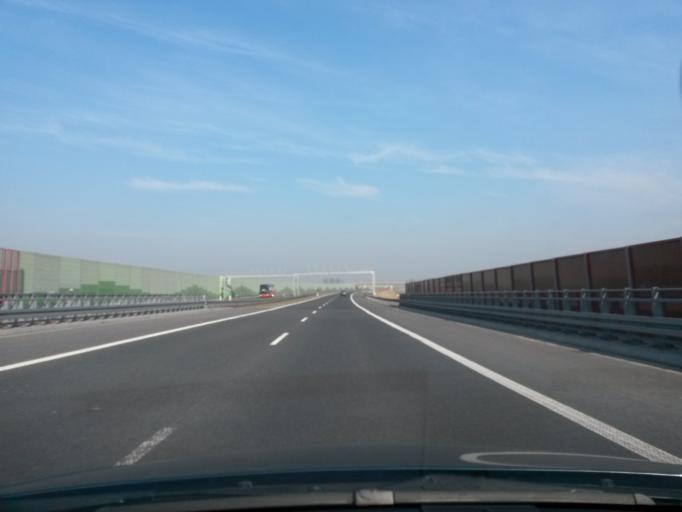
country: PL
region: Lodz Voivodeship
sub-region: Powiat kutnowski
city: Krzyzanow
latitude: 52.1414
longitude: 19.4832
